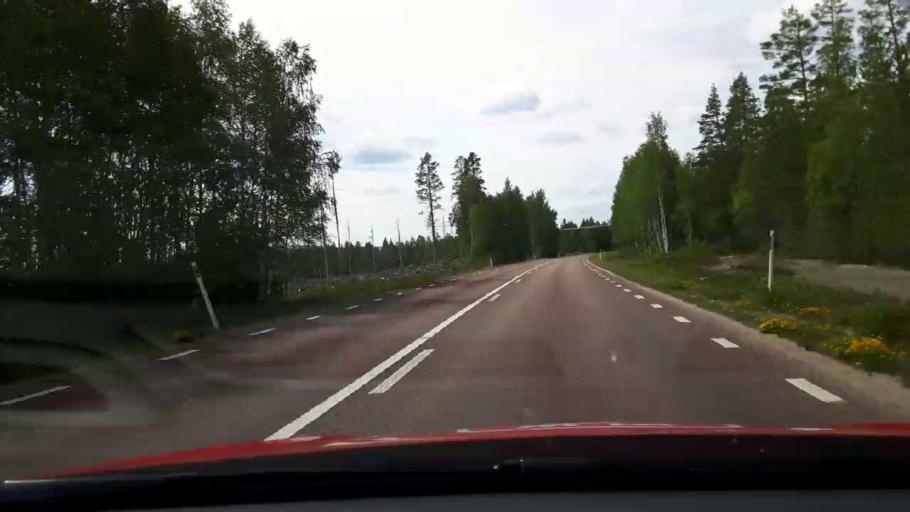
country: SE
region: Jaemtland
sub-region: Harjedalens Kommun
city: Sveg
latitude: 62.0482
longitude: 14.8871
